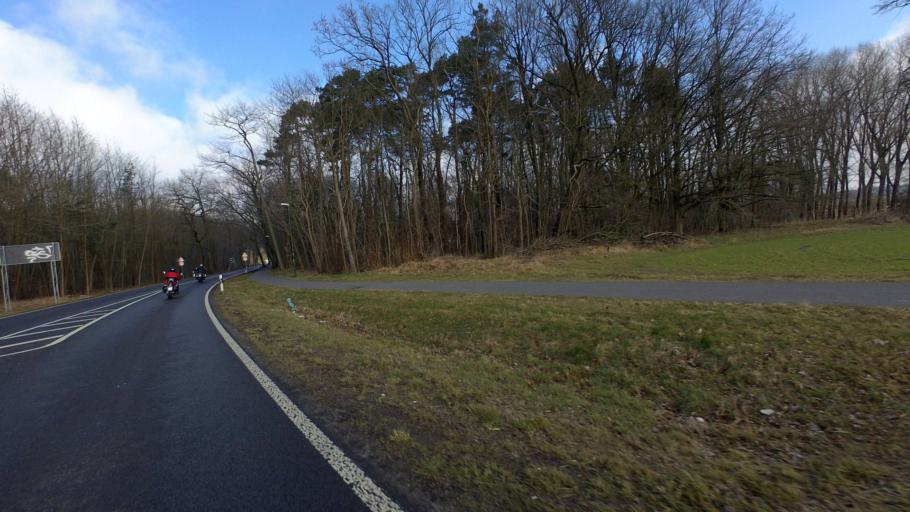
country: DE
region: Brandenburg
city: Glienicke
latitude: 52.6617
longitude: 13.3262
